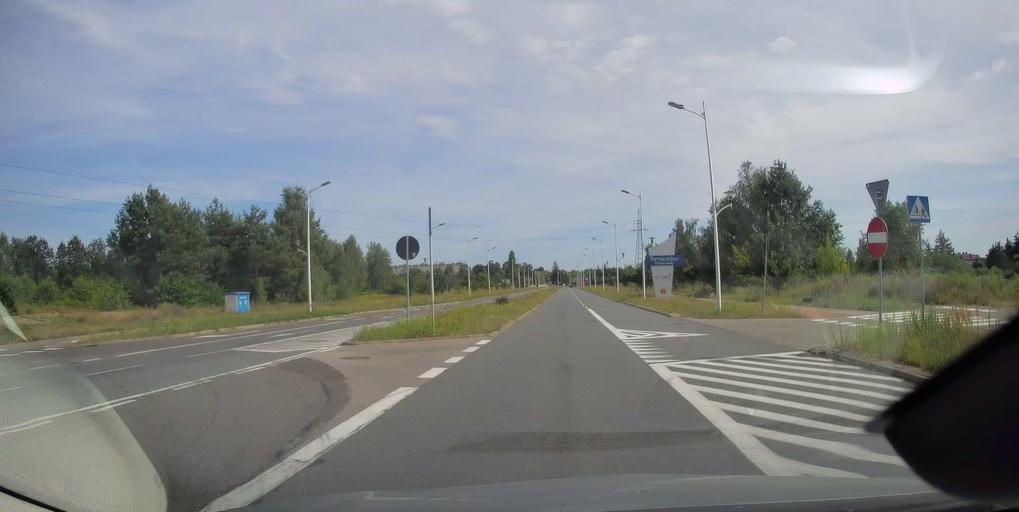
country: PL
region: Lodz Voivodeship
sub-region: Powiat tomaszowski
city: Tomaszow Mazowiecki
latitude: 51.5469
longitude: 19.9915
